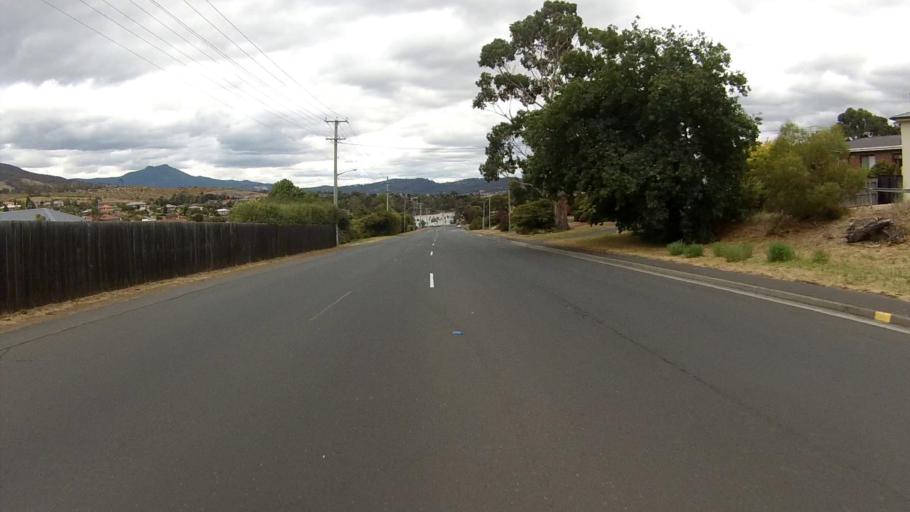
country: AU
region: Tasmania
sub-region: Glenorchy
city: Austins Ferry
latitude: -42.7687
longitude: 147.2452
